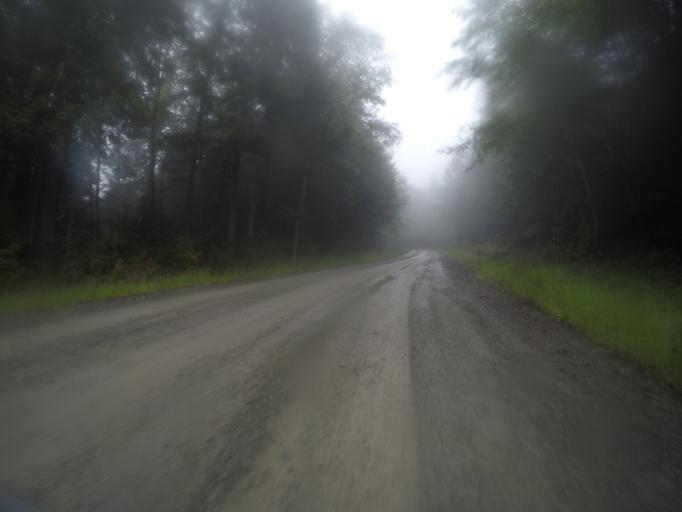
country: US
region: California
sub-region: Humboldt County
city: Westhaven-Moonstone
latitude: 41.2430
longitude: -123.9892
